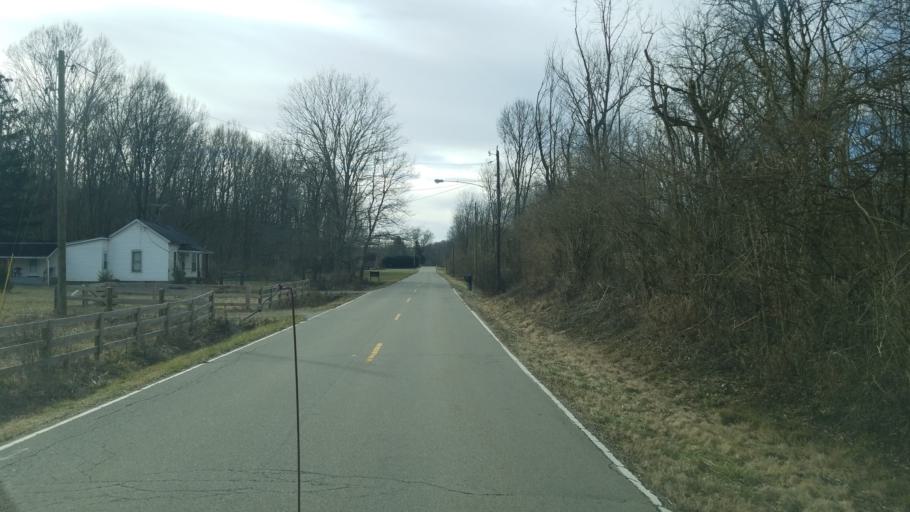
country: US
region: Ohio
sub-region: Warren County
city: Waynesville
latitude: 39.4479
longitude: -84.0977
